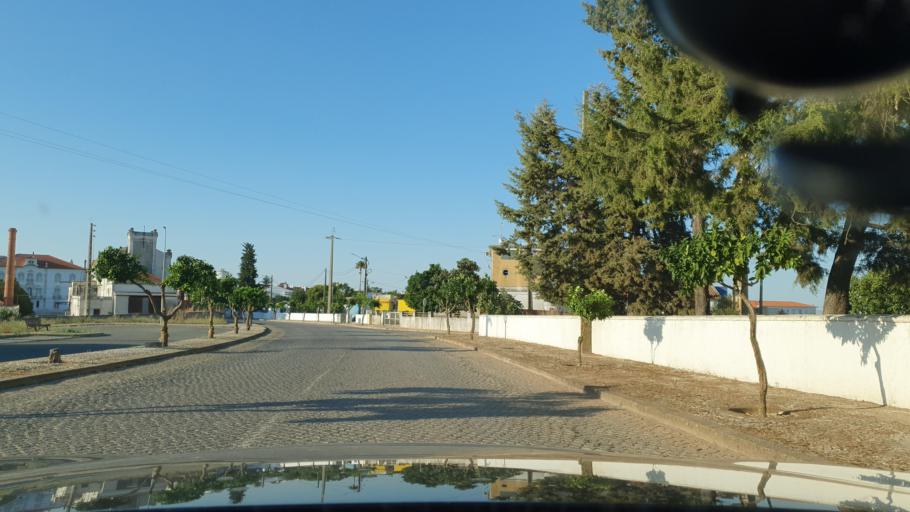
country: PT
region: Portalegre
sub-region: Fronteira
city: Fronteira
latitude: 38.9479
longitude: -7.6759
